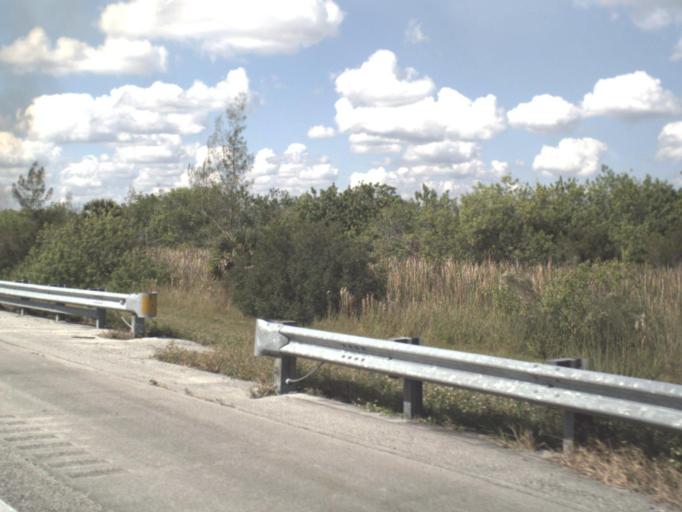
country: US
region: Florida
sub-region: Saint Lucie County
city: Lakewood Park
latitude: 27.4851
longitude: -80.5245
